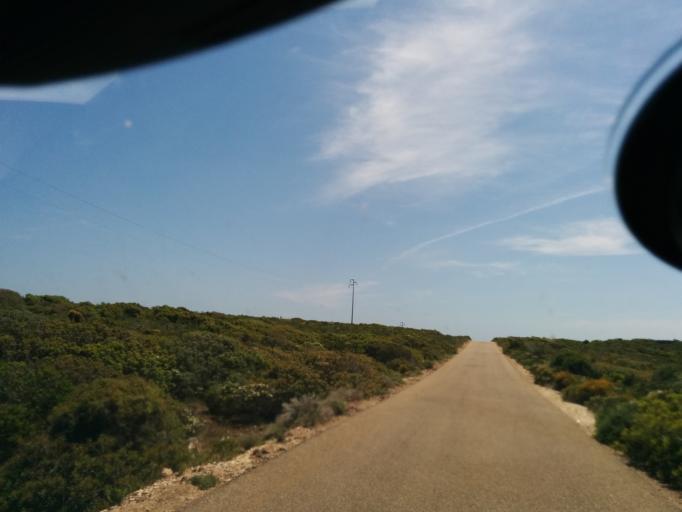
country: IT
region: Sardinia
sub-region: Provincia di Carbonia-Iglesias
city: Calasetta
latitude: 39.0318
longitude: 8.3747
